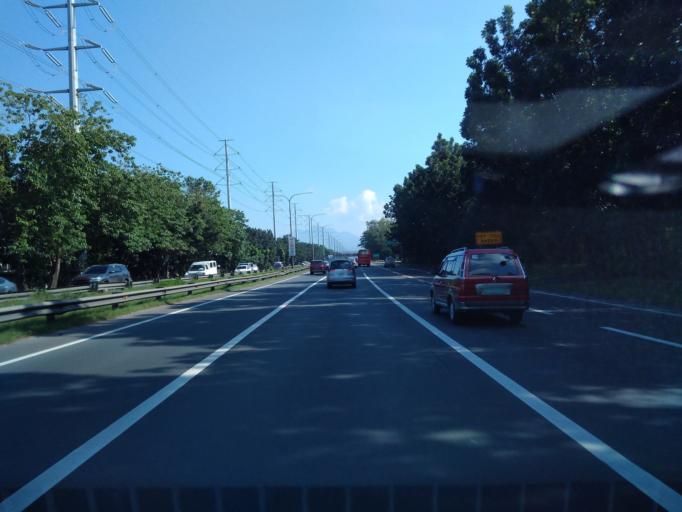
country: PH
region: Calabarzon
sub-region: Province of Laguna
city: Cabuyao
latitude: 14.2447
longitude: 121.1094
